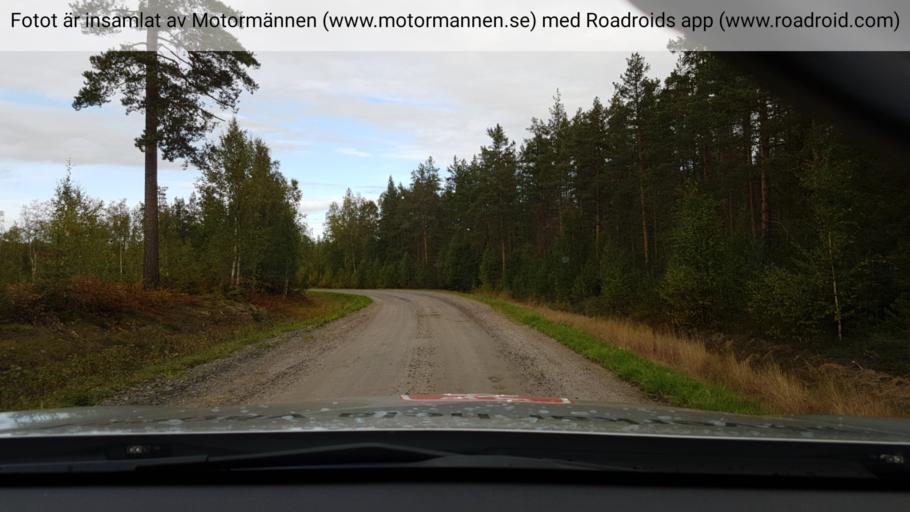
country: SE
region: Vaesterbotten
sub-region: Skelleftea Kommun
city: Byske
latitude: 65.1270
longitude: 21.2035
